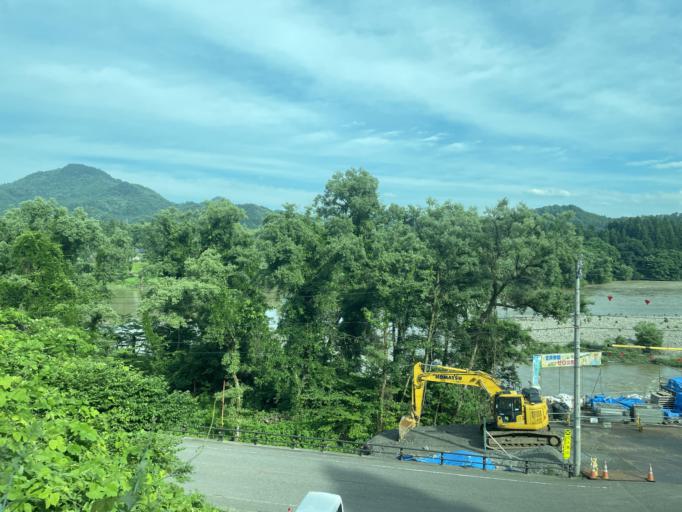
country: JP
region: Niigata
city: Suibara
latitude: 37.6898
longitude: 139.4693
